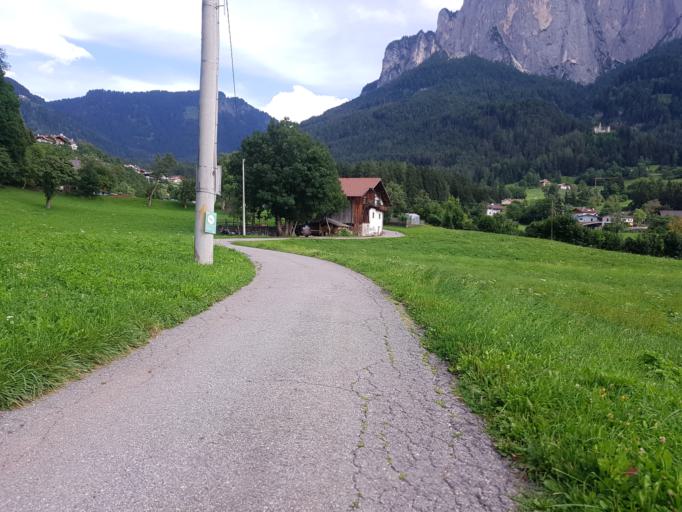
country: IT
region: Trentino-Alto Adige
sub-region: Bolzano
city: Siusi
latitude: 46.5445
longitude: 11.5527
